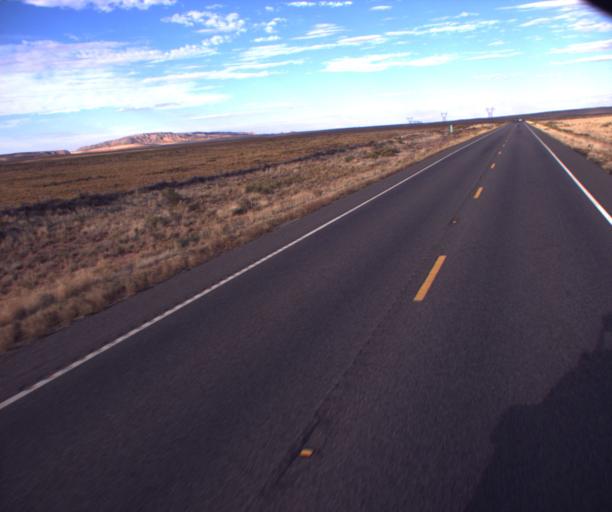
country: US
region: Arizona
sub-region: Apache County
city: Lukachukai
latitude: 36.9336
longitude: -109.2291
